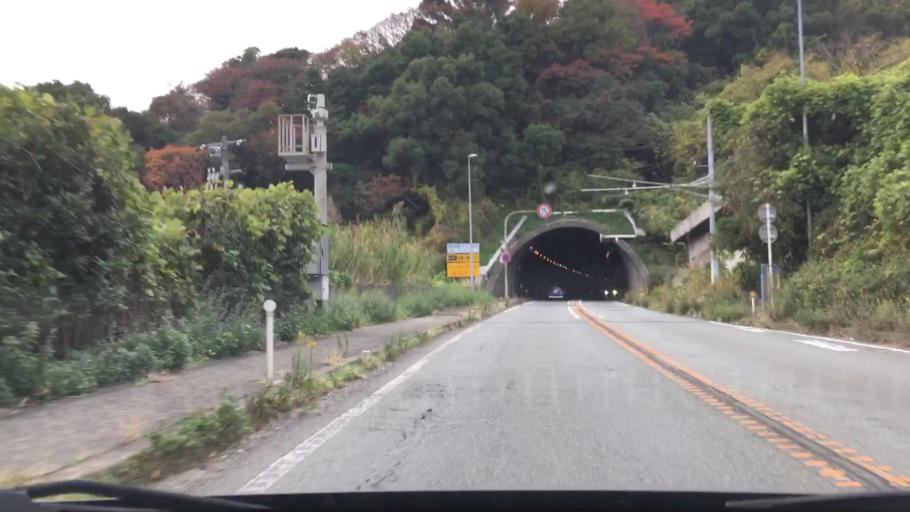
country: JP
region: Yamaguchi
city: Hofu
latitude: 34.0490
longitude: 131.6365
